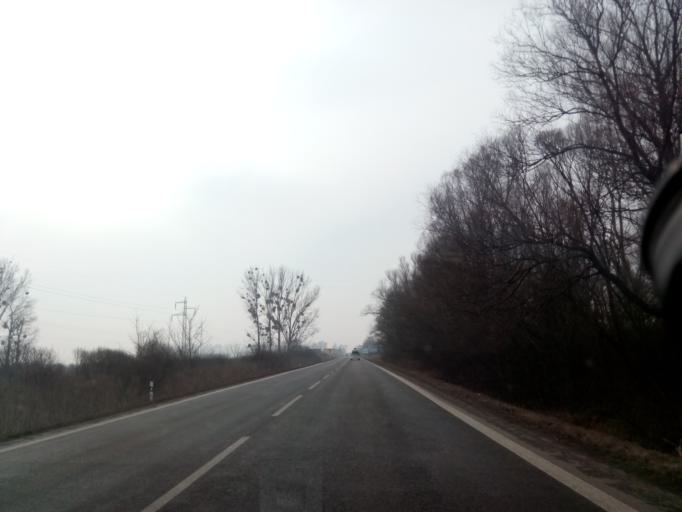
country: SK
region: Kosicky
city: Kosice
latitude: 48.6629
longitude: 21.2717
